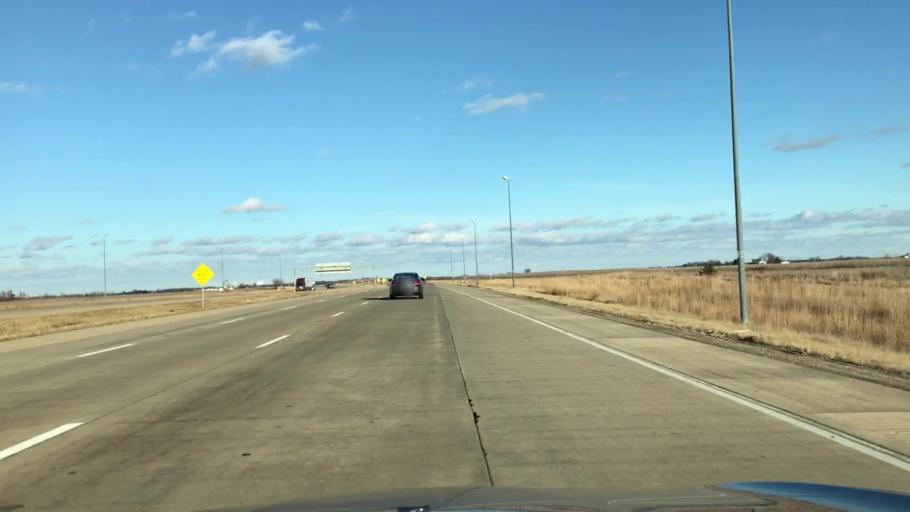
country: US
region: Illinois
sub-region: McLean County
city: Normal
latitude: 40.5388
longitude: -88.9408
